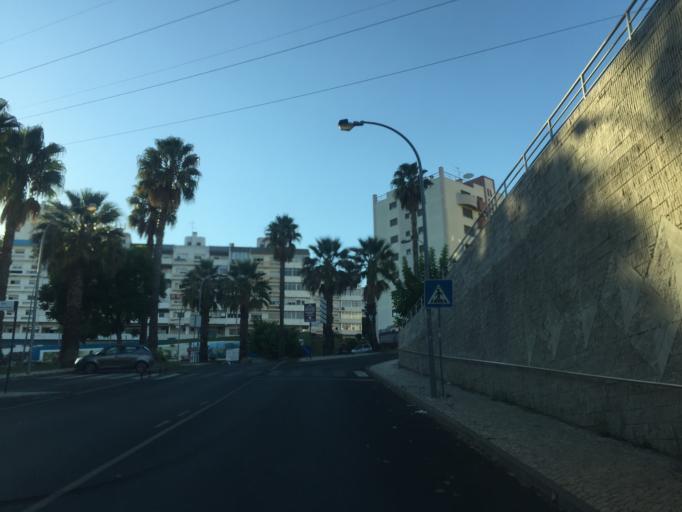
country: PT
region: Lisbon
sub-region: Odivelas
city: Odivelas
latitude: 38.7980
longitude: -9.1782
